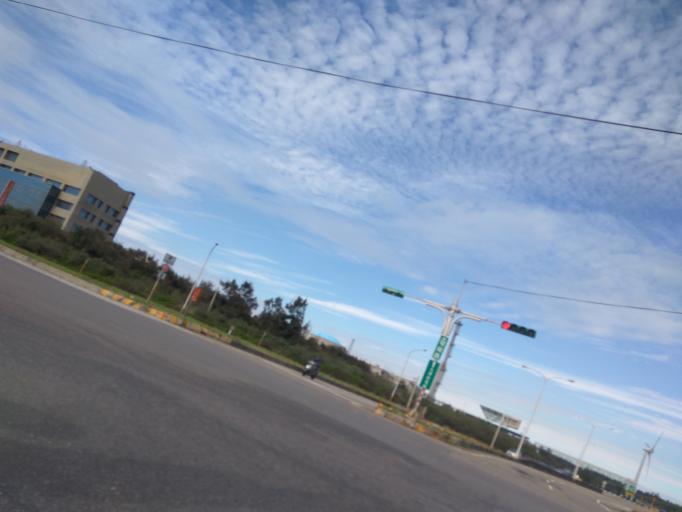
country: TW
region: Taiwan
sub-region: Hsinchu
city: Zhubei
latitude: 25.0297
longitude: 121.0531
